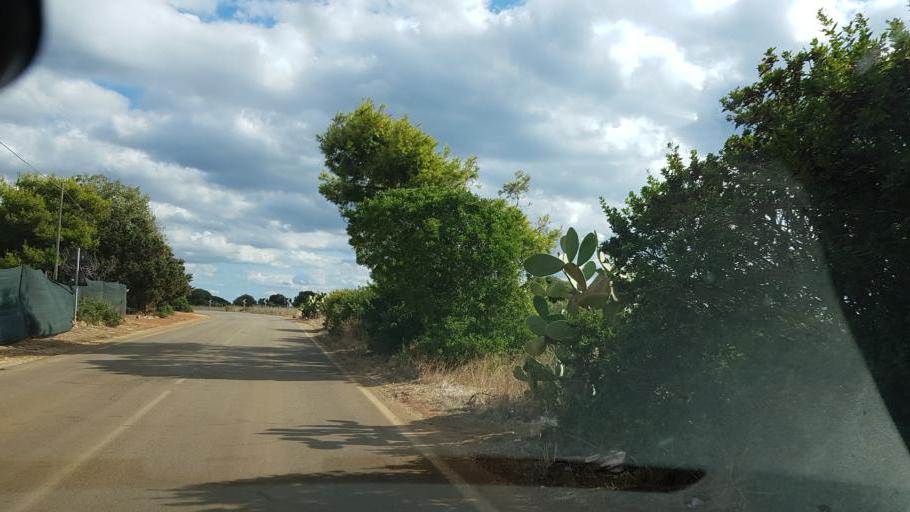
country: IT
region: Apulia
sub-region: Provincia di Lecce
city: Nardo
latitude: 40.1607
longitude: 17.9548
